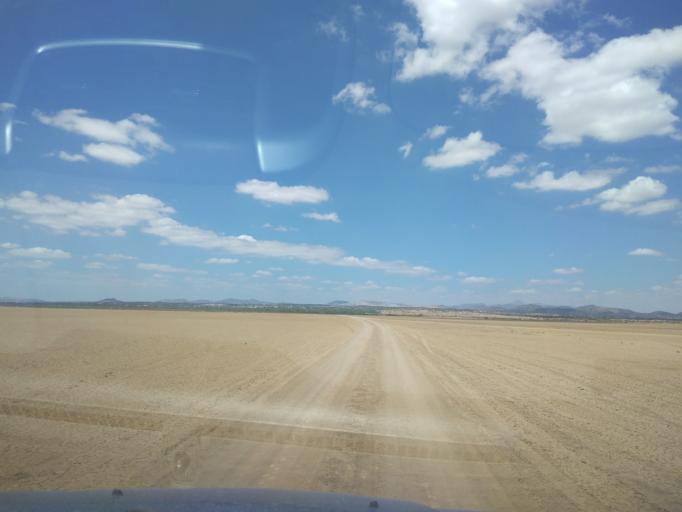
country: TN
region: Susah
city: Harqalah
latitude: 36.1620
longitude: 10.4577
